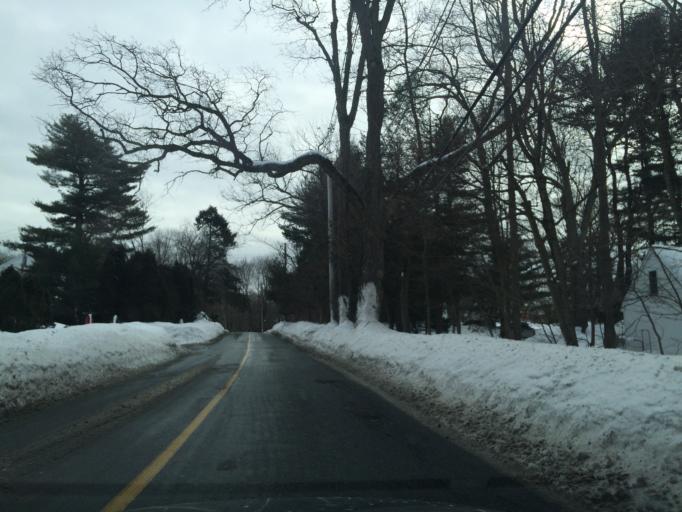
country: US
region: Massachusetts
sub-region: Middlesex County
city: Weston
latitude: 42.3431
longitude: -71.2789
